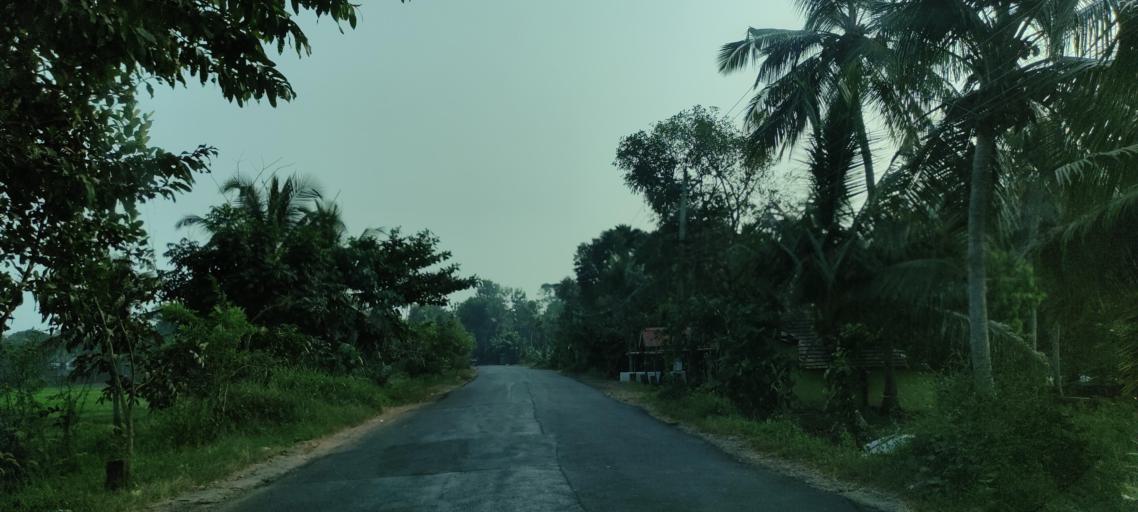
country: IN
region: Kerala
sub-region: Kottayam
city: Vaikam
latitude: 9.6910
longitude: 76.4637
